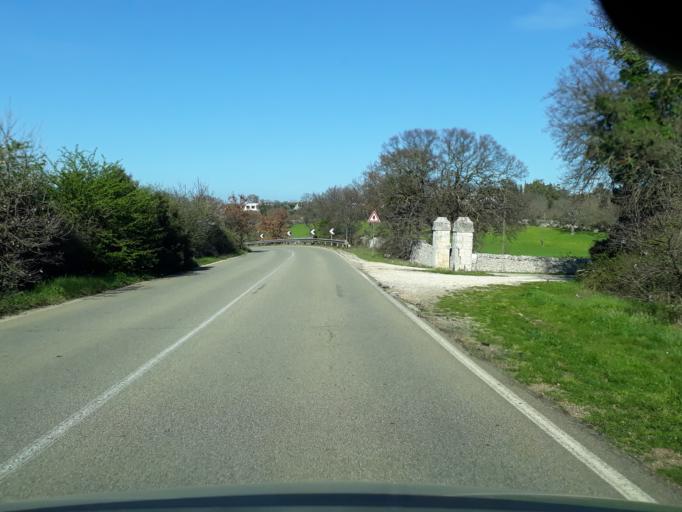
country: IT
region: Apulia
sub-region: Provincia di Bari
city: Cozzana
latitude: 40.8558
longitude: 17.2552
